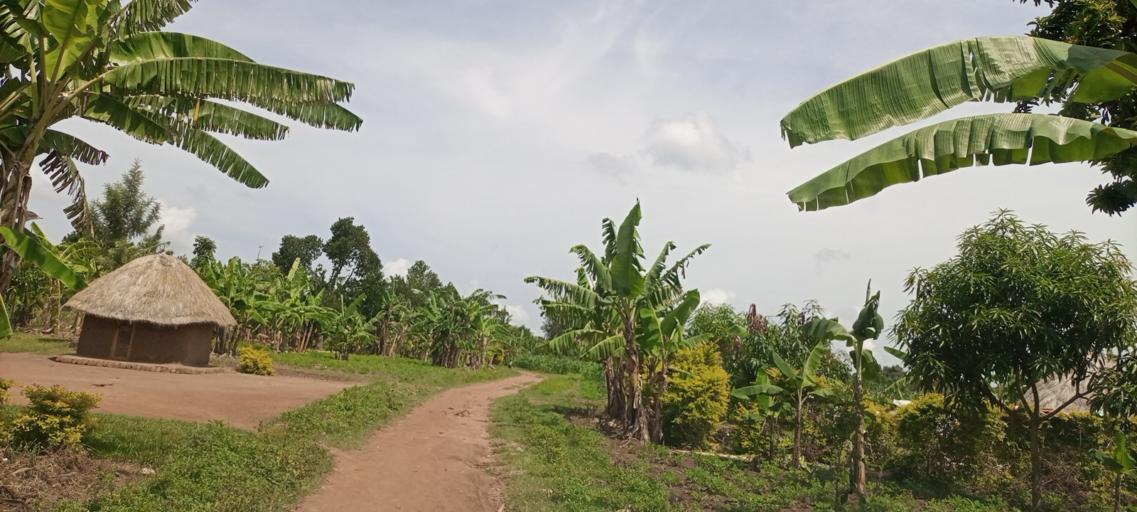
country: UG
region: Eastern Region
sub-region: Budaka District
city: Budaka
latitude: 1.1715
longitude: 33.9481
